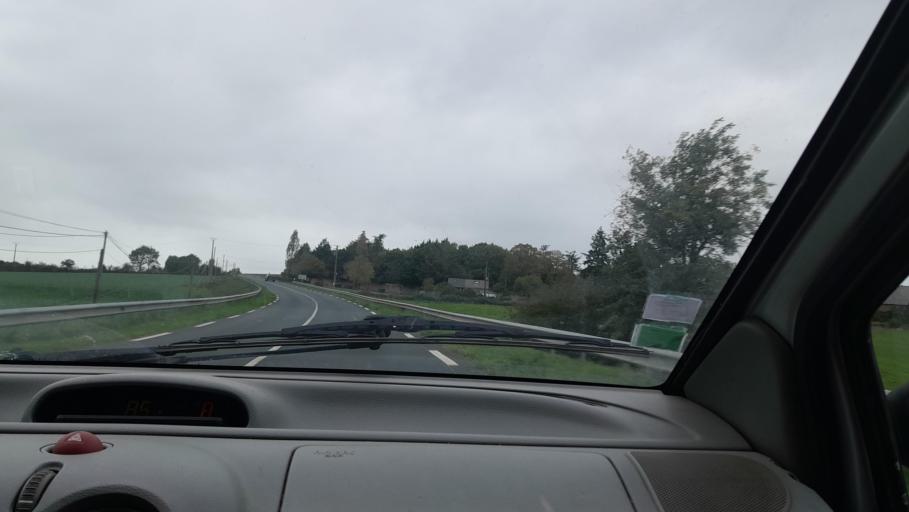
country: FR
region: Pays de la Loire
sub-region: Departement de la Loire-Atlantique
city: Saint-Mars-la-Jaille
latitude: 47.5017
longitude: -1.1772
